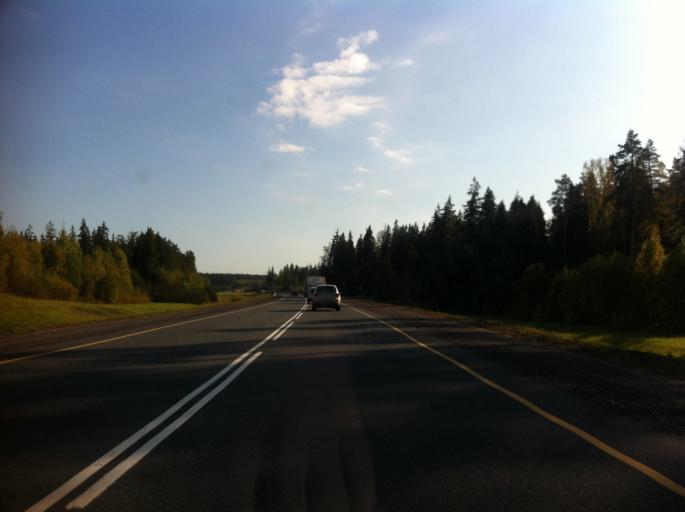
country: RU
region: Leningrad
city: Luga
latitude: 58.7625
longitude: 29.8834
